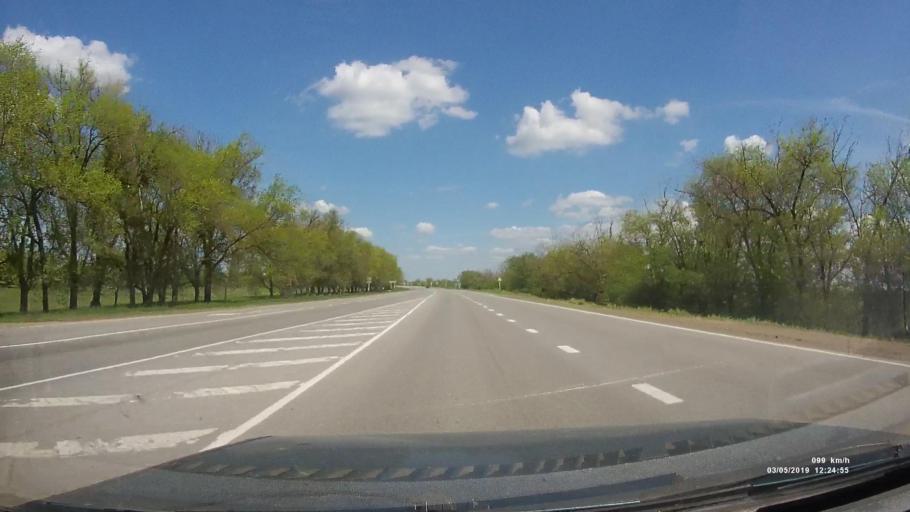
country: RU
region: Rostov
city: Semikarakorsk
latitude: 47.4255
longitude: 40.7064
